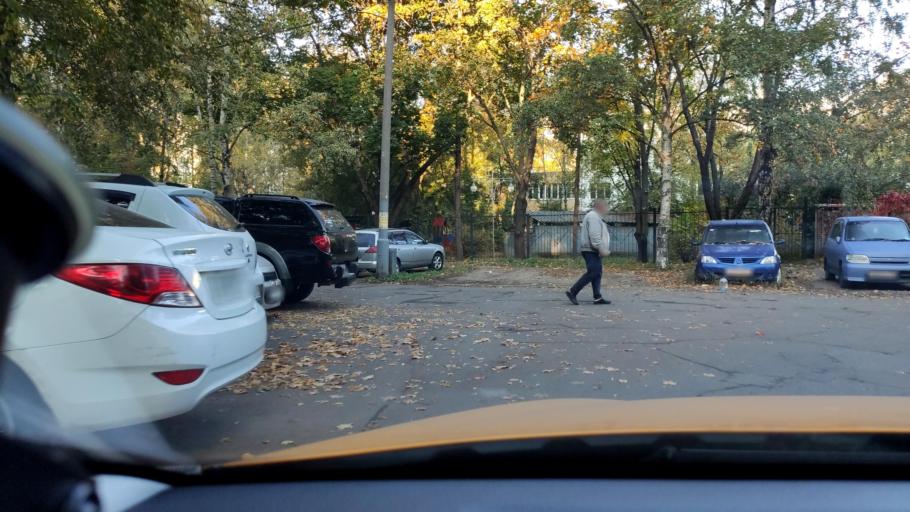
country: RU
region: Moscow
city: Vykhino-Zhulebino
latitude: 55.6961
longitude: 37.8244
